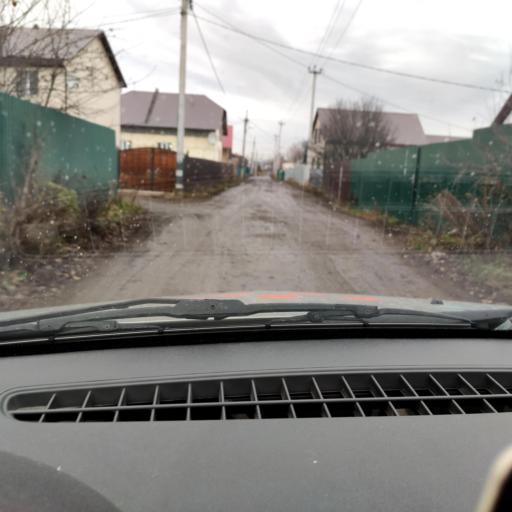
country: RU
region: Bashkortostan
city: Mikhaylovka
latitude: 54.8399
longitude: 55.9465
